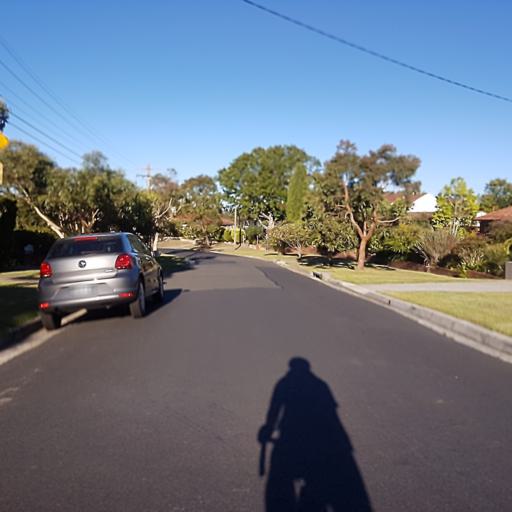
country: AU
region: New South Wales
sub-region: Ku-ring-gai
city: Roseville Chase
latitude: -33.7812
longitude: 151.2030
